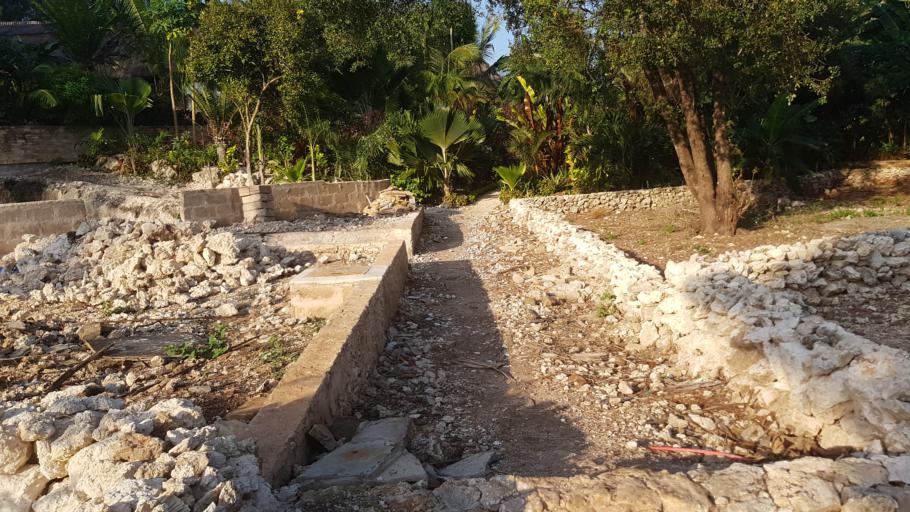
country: TZ
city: Kiwengwa
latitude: -6.0343
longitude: 39.4062
